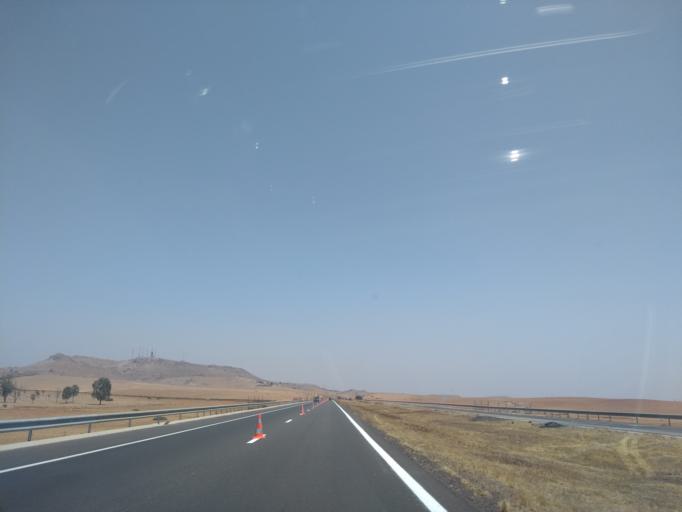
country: MA
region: Marrakech-Tensift-Al Haouz
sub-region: Kelaa-Des-Sraghna
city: Sidi Abdallah
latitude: 32.4501
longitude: -7.9315
